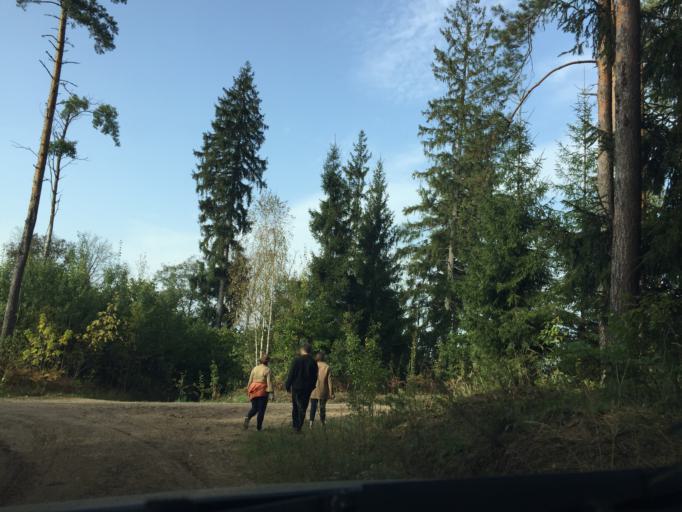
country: LV
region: Garkalne
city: Garkalne
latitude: 56.9735
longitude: 24.4321
